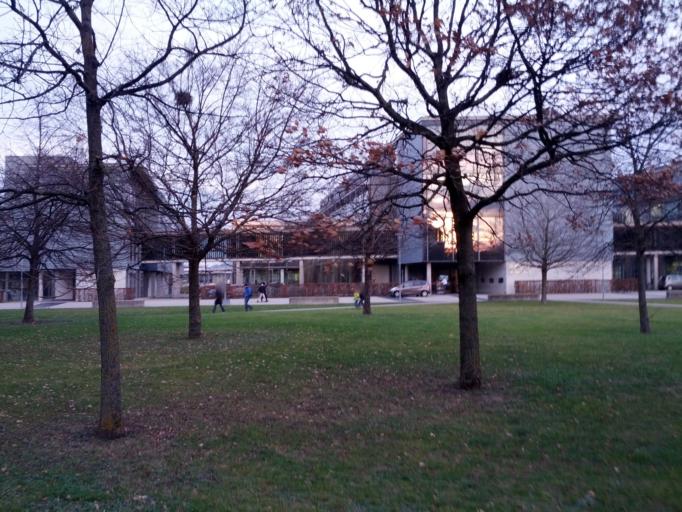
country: DE
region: Baden-Wuerttemberg
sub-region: Freiburg Region
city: Freiburg
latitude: 48.0132
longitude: 7.8342
